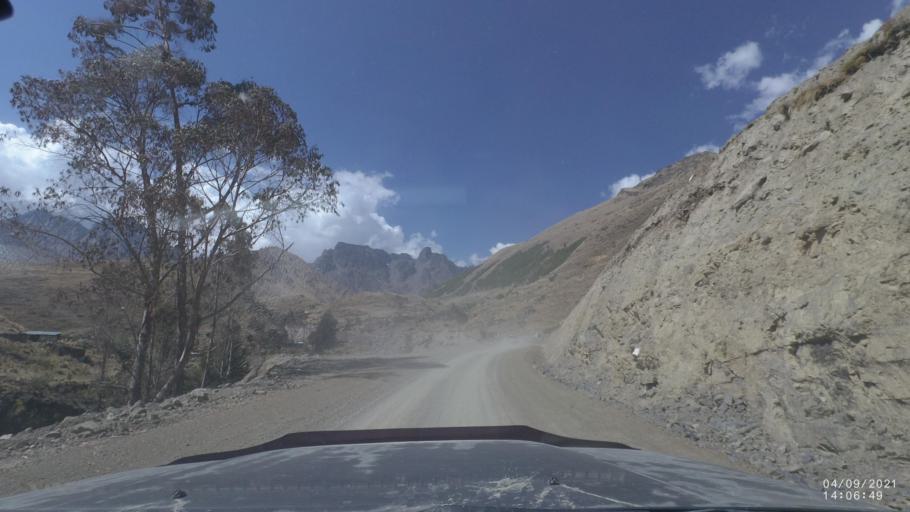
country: BO
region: Cochabamba
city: Sipe Sipe
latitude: -17.2293
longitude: -66.4694
